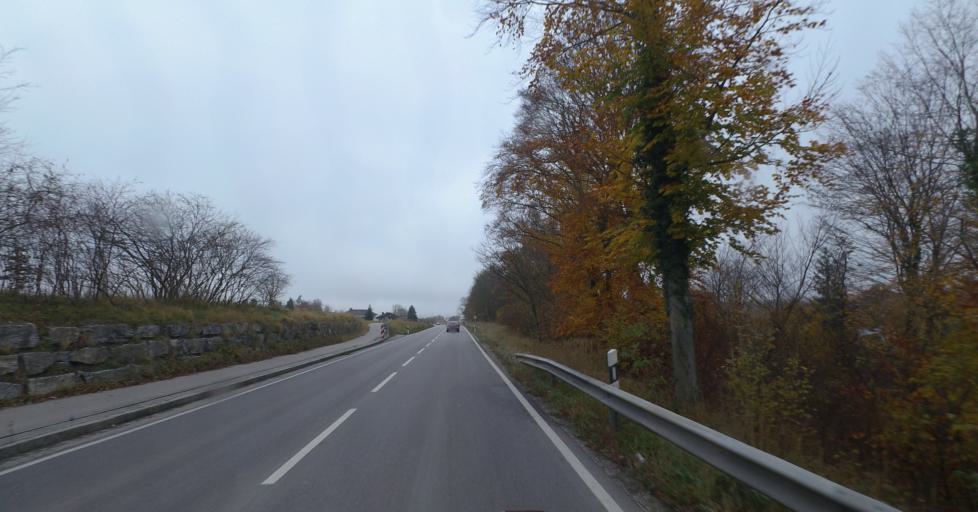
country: DE
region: Bavaria
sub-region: Upper Bavaria
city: Trostberg an der Alz
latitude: 48.0518
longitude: 12.5678
